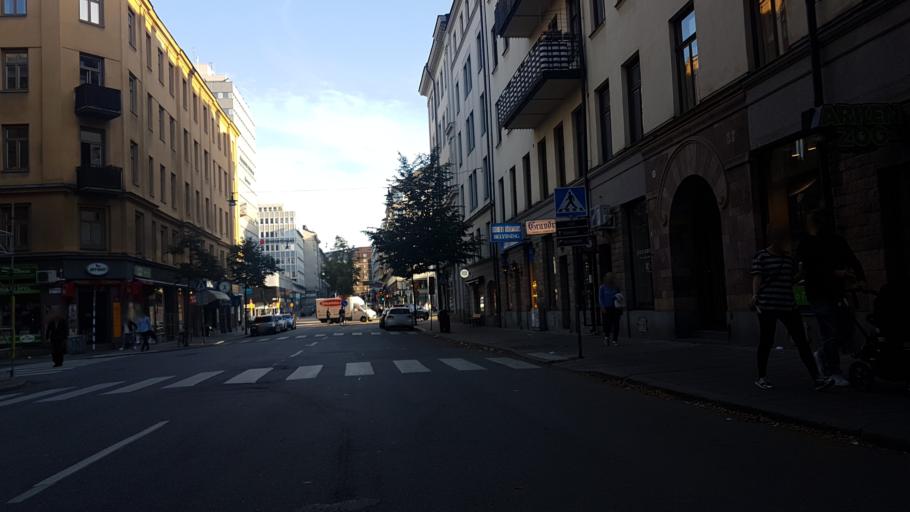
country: SE
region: Stockholm
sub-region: Stockholms Kommun
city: Stockholm
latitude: 59.3438
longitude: 18.0501
